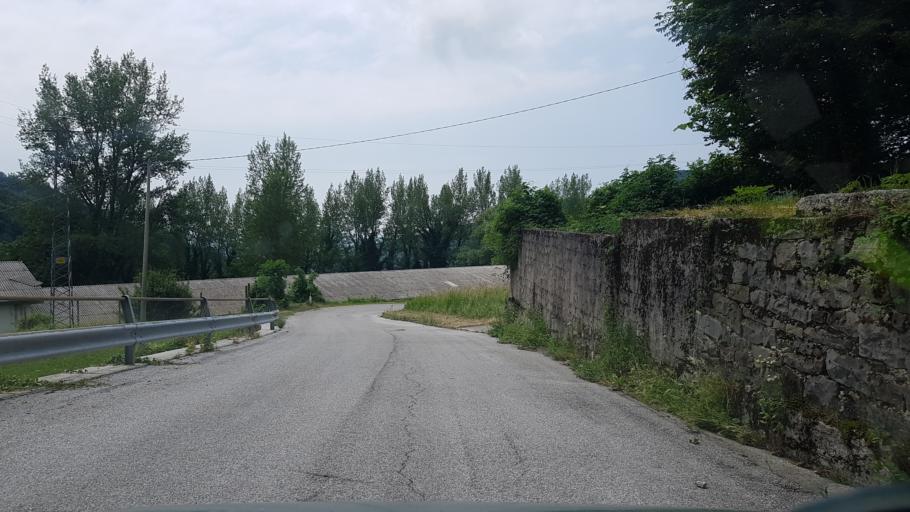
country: IT
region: Friuli Venezia Giulia
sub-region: Provincia di Udine
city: Torreano
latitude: 46.1715
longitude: 13.4329
